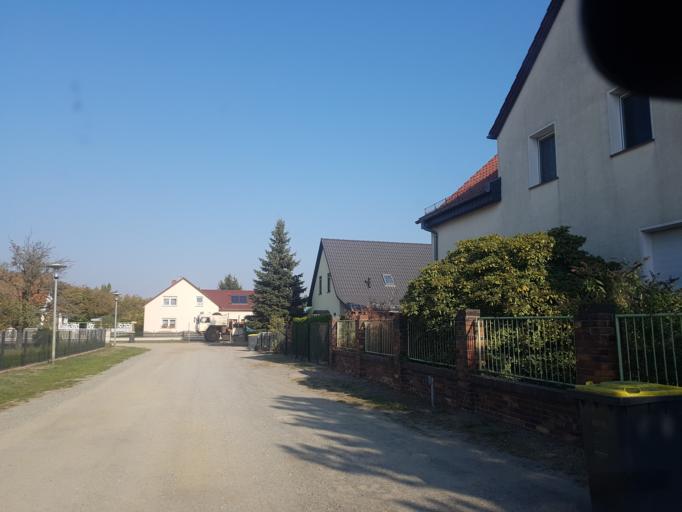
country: DE
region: Brandenburg
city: Finsterwalde
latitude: 51.6182
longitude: 13.7177
